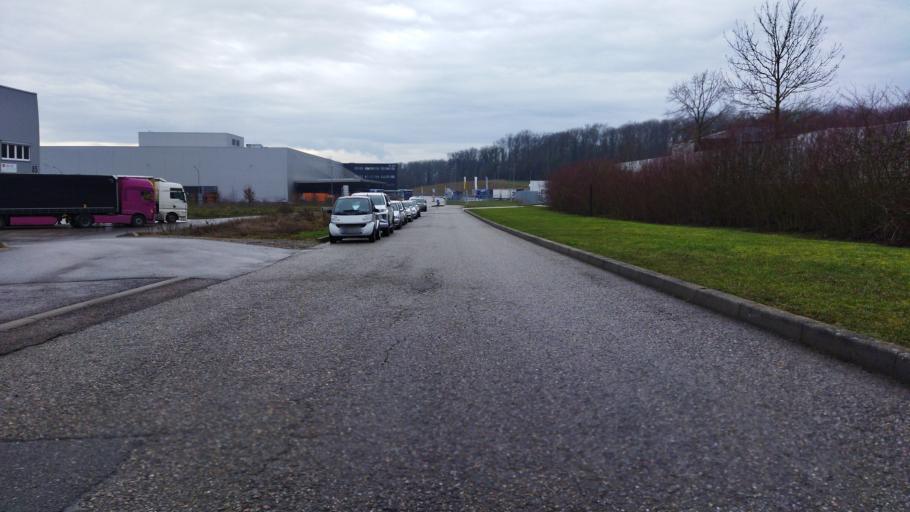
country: DE
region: Baden-Wuerttemberg
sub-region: Regierungsbezirk Stuttgart
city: Bad Wimpfen
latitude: 49.1815
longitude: 9.1622
